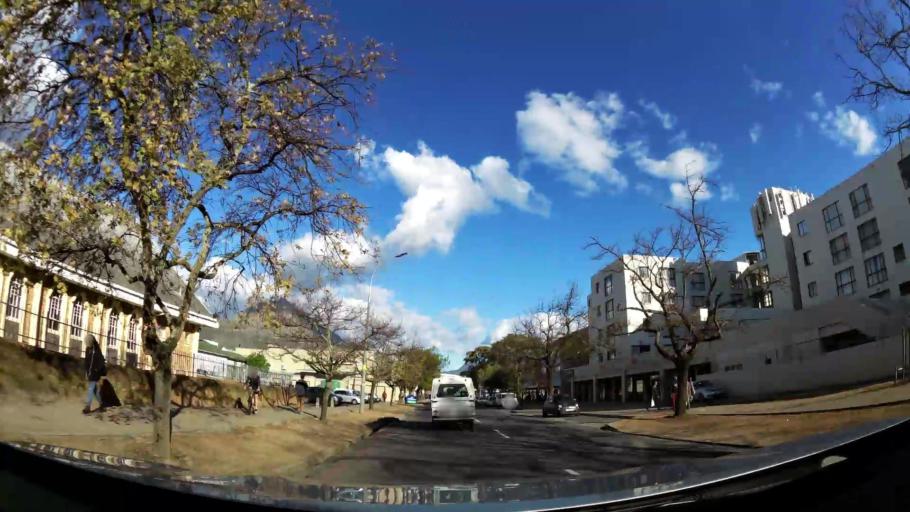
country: ZA
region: Western Cape
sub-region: Cape Winelands District Municipality
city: Stellenbosch
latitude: -33.9307
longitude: 18.8577
